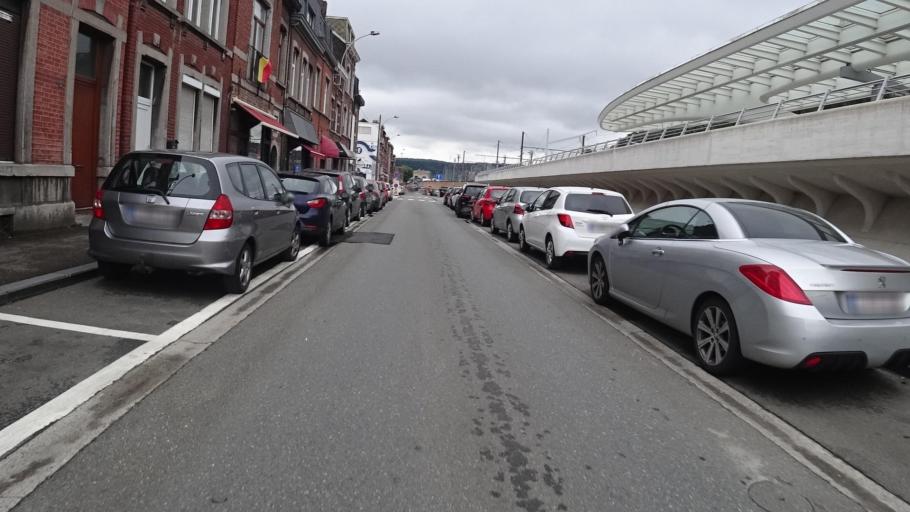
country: BE
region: Wallonia
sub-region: Province de Liege
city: Liege
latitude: 50.6229
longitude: 5.5695
